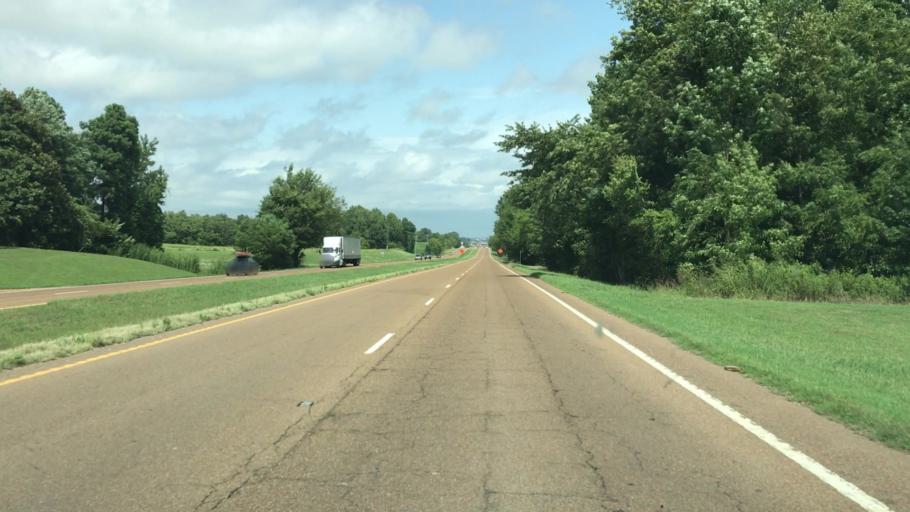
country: US
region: Tennessee
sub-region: Obion County
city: Englewood
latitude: 36.3770
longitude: -89.1157
